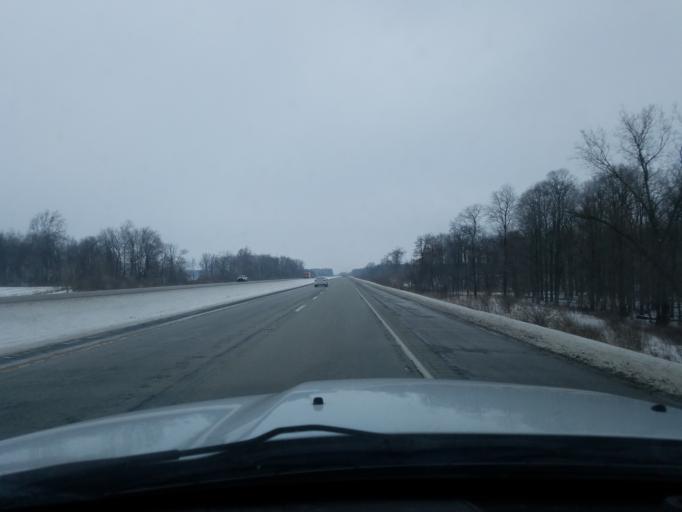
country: US
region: Indiana
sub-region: Fulton County
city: Rochester
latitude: 41.1471
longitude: -86.2396
